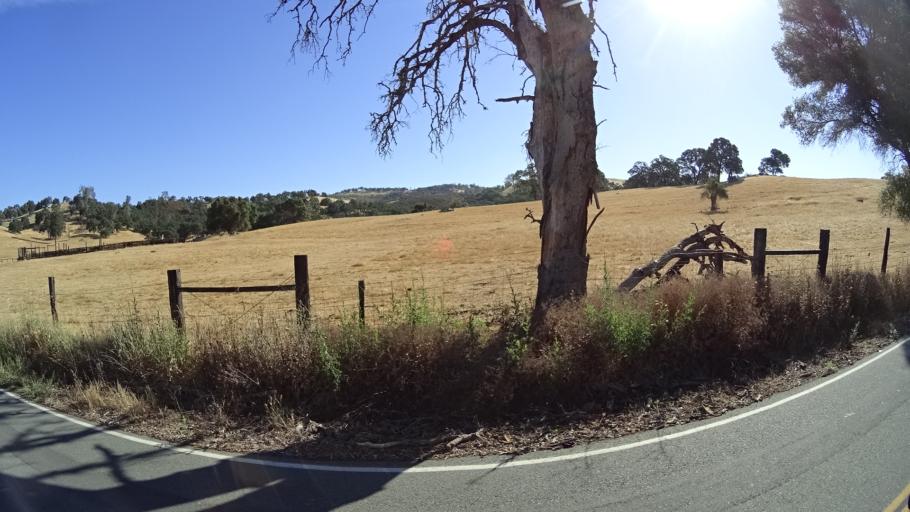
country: US
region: California
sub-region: Calaveras County
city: San Andreas
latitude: 38.1727
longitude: -120.6421
